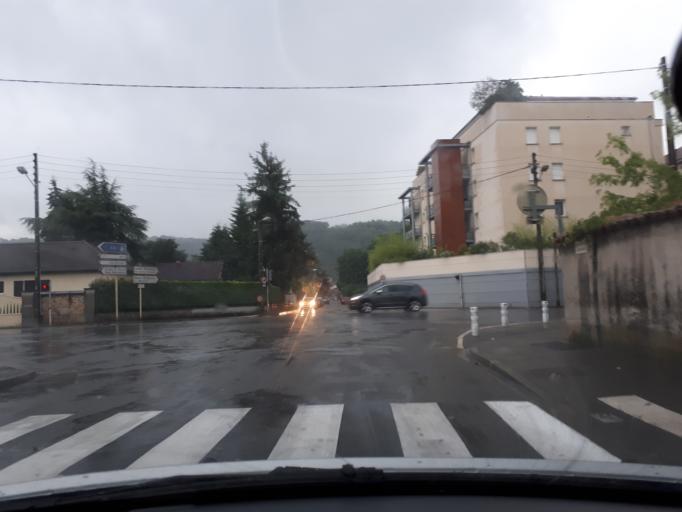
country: FR
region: Rhone-Alpes
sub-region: Departement de l'Isere
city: Bourgoin
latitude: 45.5892
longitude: 5.2842
